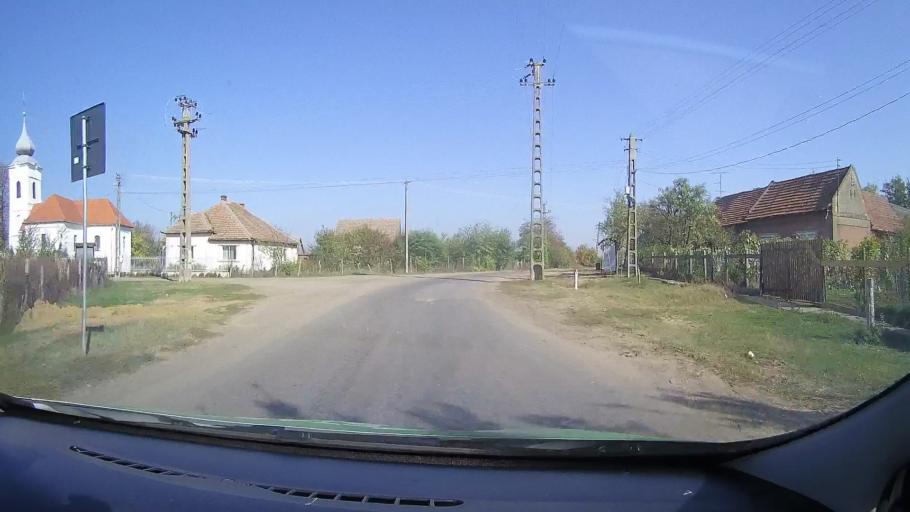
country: RO
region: Satu Mare
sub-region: Comuna Ciumesti
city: Ciumesti
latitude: 47.6692
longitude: 22.3391
